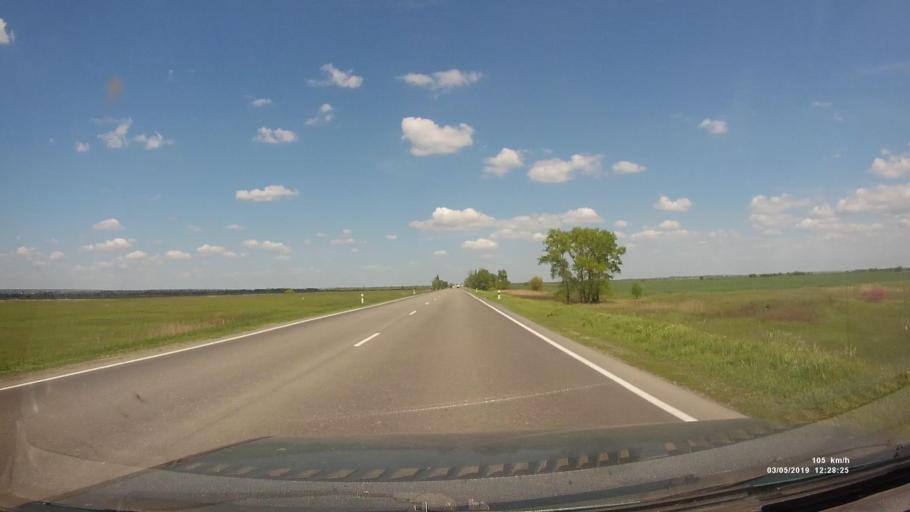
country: RU
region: Rostov
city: Semikarakorsk
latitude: 47.4733
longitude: 40.7280
